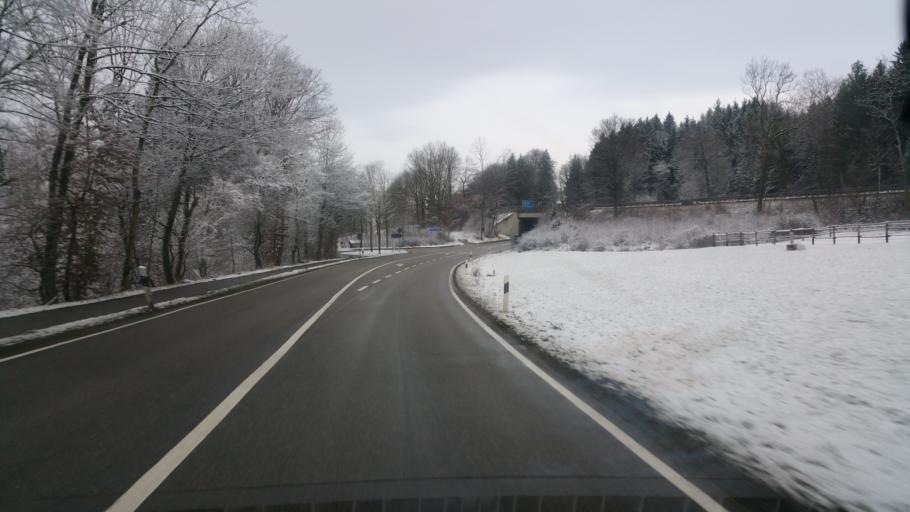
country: DE
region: Bavaria
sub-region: Upper Bavaria
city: Samerberg
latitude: 47.7956
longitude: 12.2088
